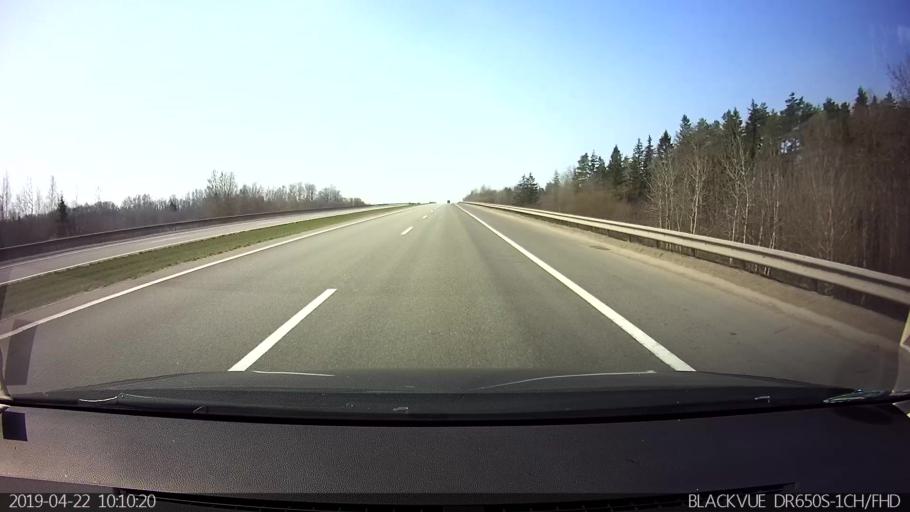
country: BY
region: Vitebsk
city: Horad Orsha
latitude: 54.6155
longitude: 30.3957
